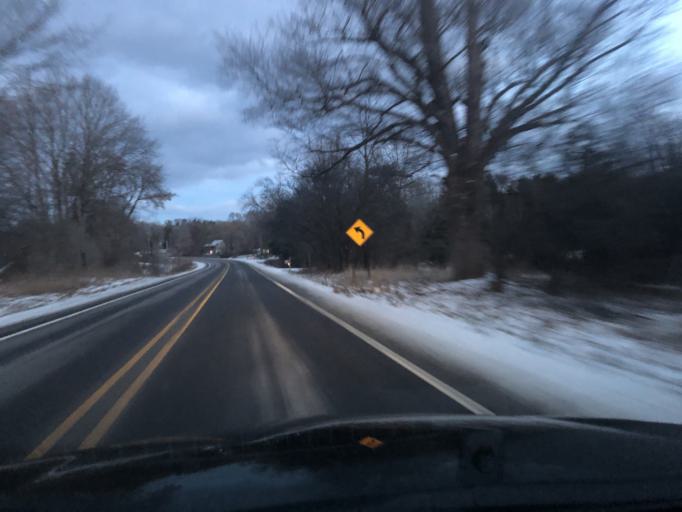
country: US
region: Michigan
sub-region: Oakland County
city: Milford
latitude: 42.5794
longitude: -83.6219
